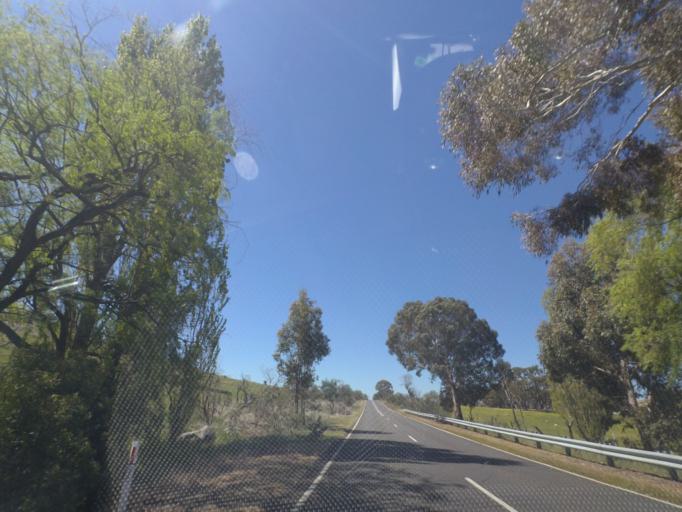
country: AU
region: Victoria
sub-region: Hume
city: Sunbury
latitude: -37.1682
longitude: 144.7562
